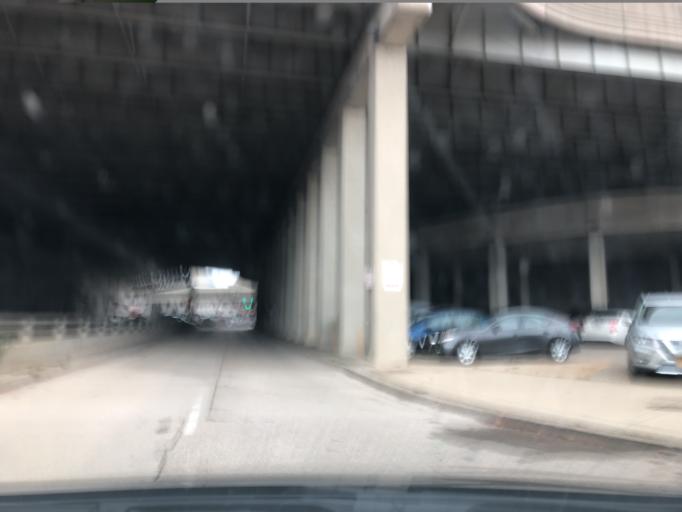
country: US
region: Kentucky
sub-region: Campbell County
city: Newport
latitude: 39.0970
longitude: -84.5051
